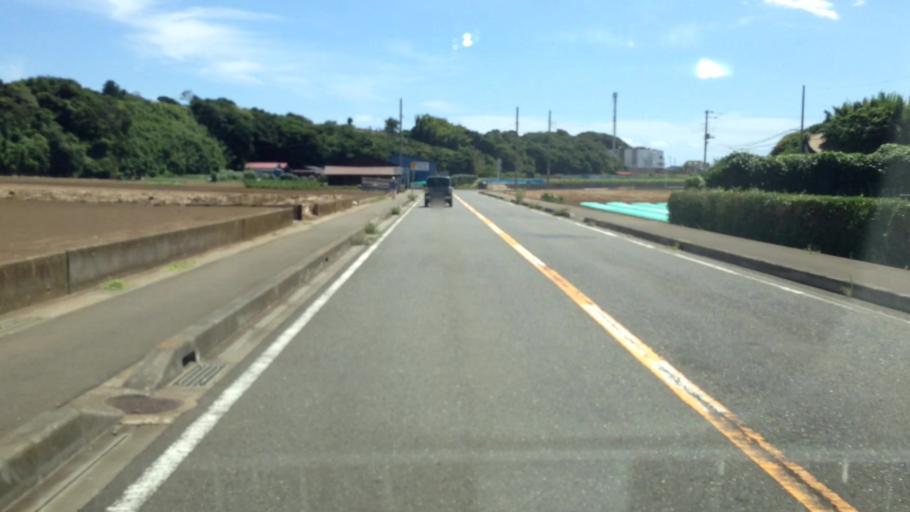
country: JP
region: Kanagawa
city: Miura
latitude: 35.1982
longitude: 139.6190
